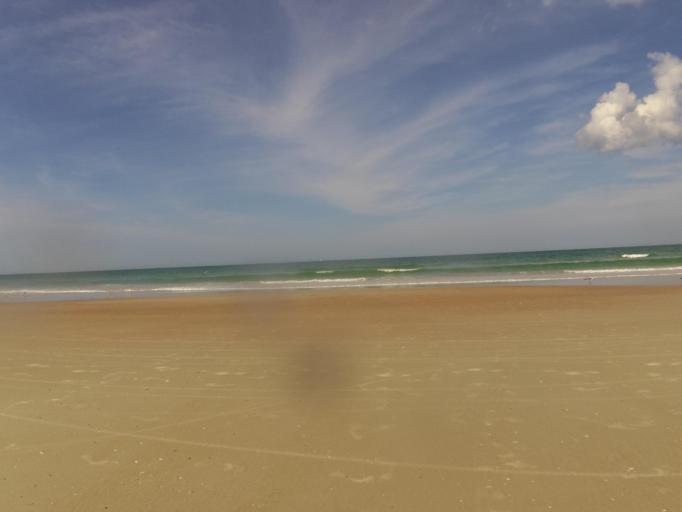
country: US
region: Florida
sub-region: Volusia County
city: Ponce Inlet
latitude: 29.0917
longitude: -80.9299
